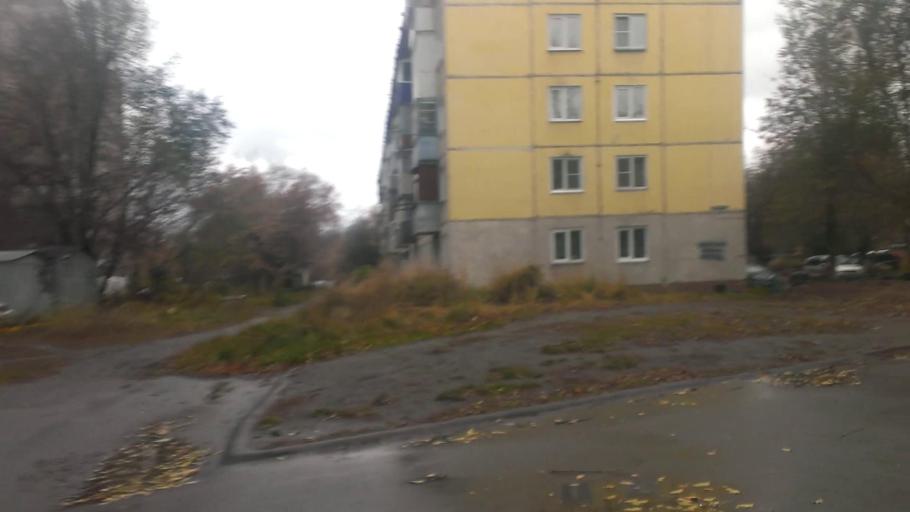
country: RU
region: Altai Krai
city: Novosilikatnyy
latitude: 53.3522
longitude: 83.6865
